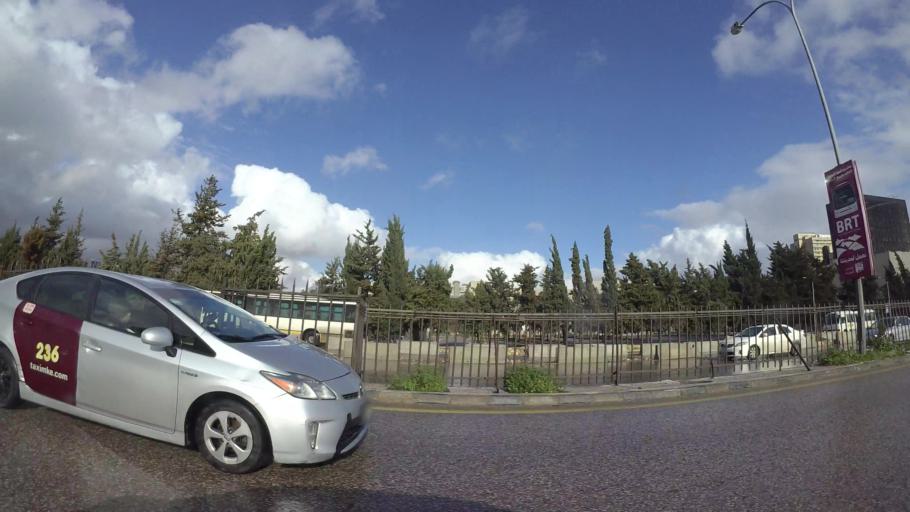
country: JO
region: Amman
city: Al Jubayhah
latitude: 32.0094
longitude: 35.8712
